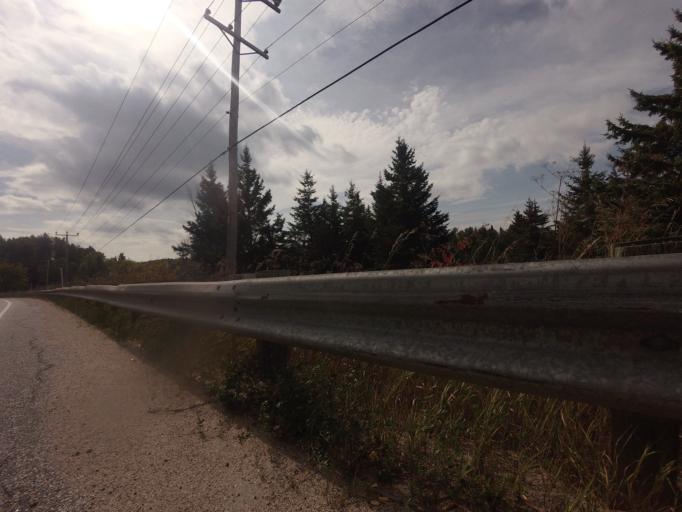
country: CA
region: Quebec
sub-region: Outaouais
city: Wakefield
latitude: 45.8514
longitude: -75.9962
